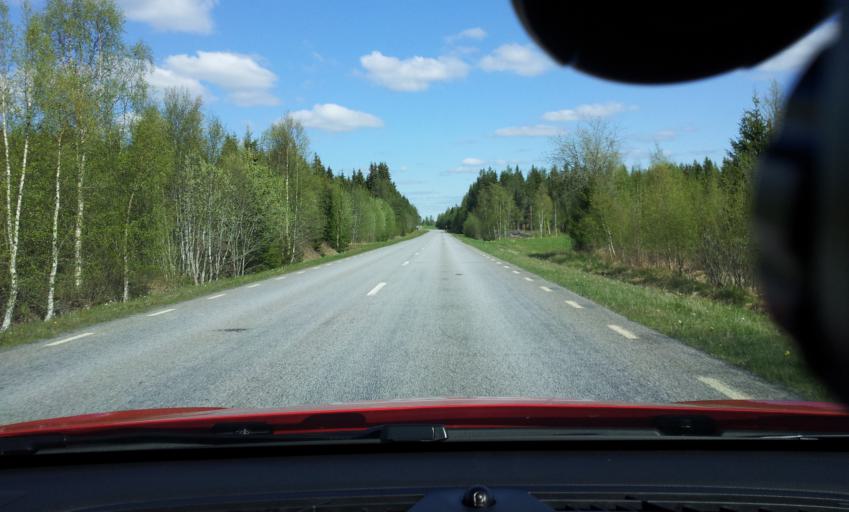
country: SE
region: Jaemtland
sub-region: Krokoms Kommun
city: Valla
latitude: 63.2311
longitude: 14.0121
